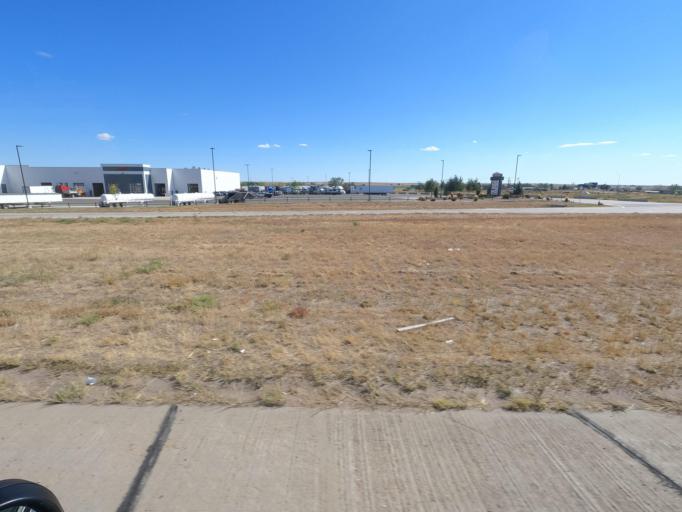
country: US
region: Colorado
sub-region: Weld County
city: Lochbuie
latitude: 39.9746
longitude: -104.7484
